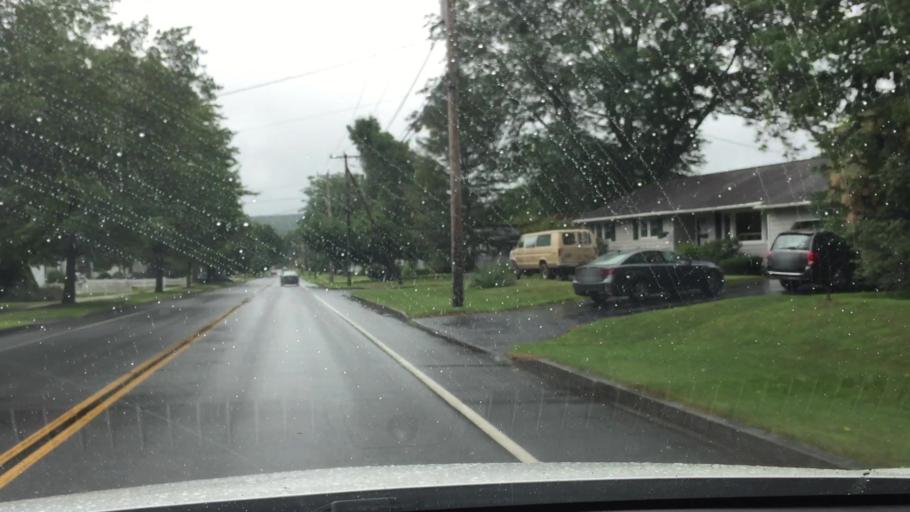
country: US
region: Massachusetts
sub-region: Berkshire County
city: Pittsfield
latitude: 42.4367
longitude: -73.2217
